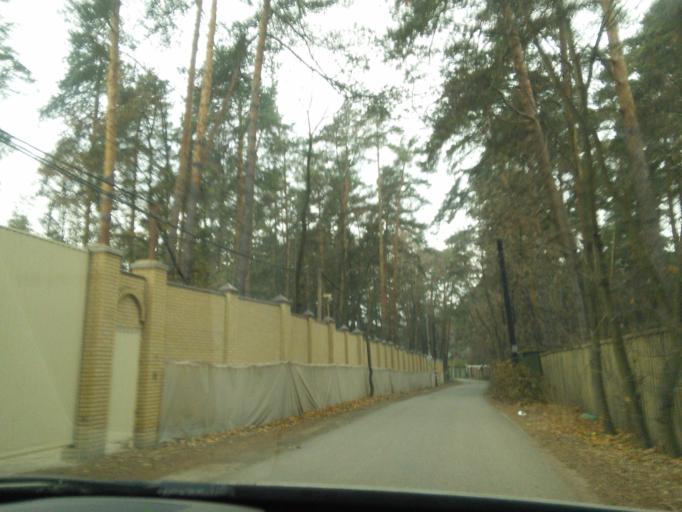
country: RU
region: Moskovskaya
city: Kraskovo
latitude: 55.6412
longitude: 37.9822
